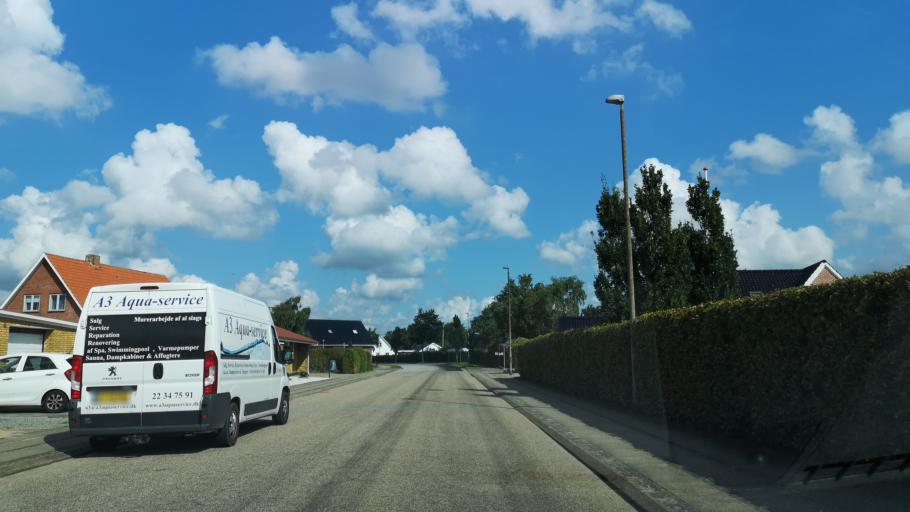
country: DK
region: Central Jutland
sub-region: Ringkobing-Skjern Kommune
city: Skjern
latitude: 55.9469
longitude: 8.4869
